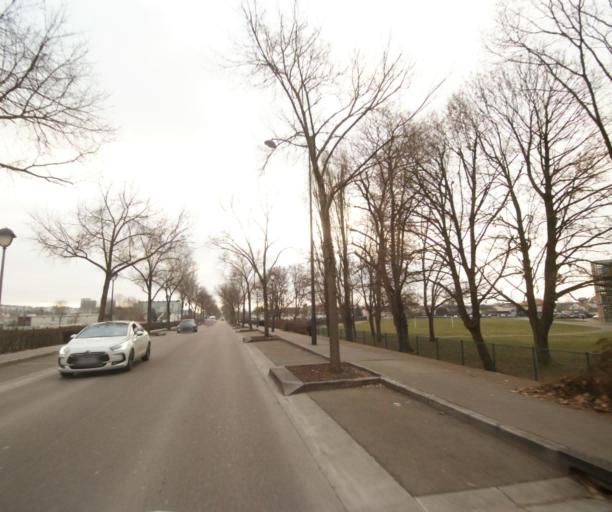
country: FR
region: Champagne-Ardenne
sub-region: Departement de la Haute-Marne
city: Bettancourt-la-Ferree
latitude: 48.6426
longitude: 4.9664
